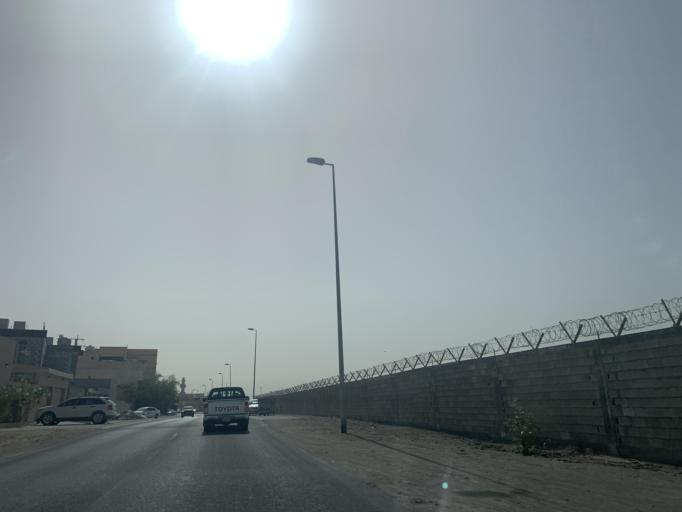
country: BH
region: Northern
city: Sitrah
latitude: 26.1555
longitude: 50.6141
